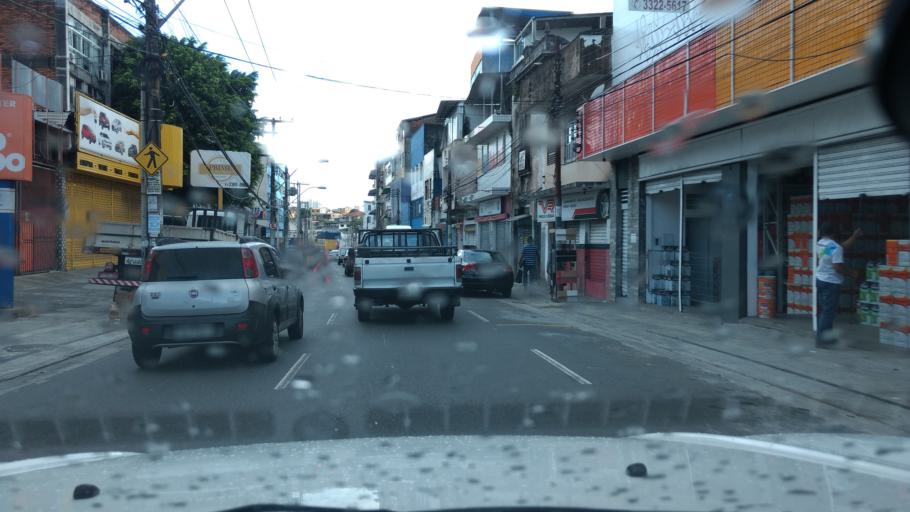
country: BR
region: Bahia
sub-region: Salvador
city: Salvador
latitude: -12.9747
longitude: -38.5000
